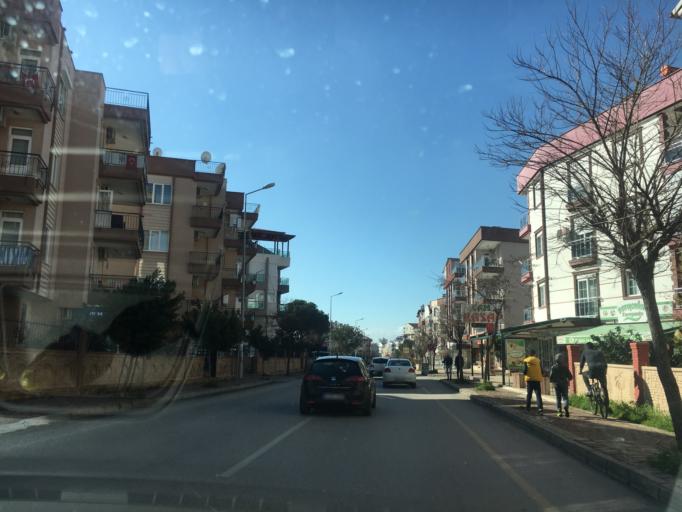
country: TR
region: Antalya
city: Antalya
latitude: 36.9176
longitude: 30.7075
